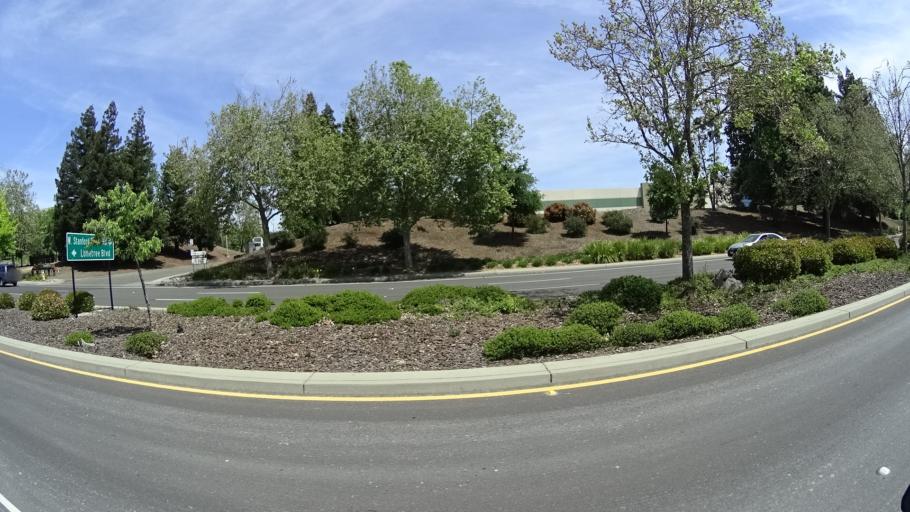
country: US
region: California
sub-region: Placer County
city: Rocklin
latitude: 38.8136
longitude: -121.2857
